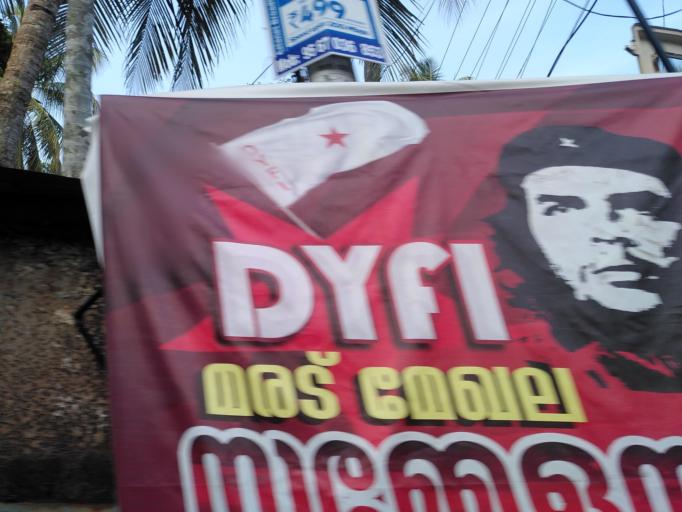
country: IN
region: Kerala
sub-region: Ernakulam
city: Cochin
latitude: 9.9343
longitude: 76.3247
